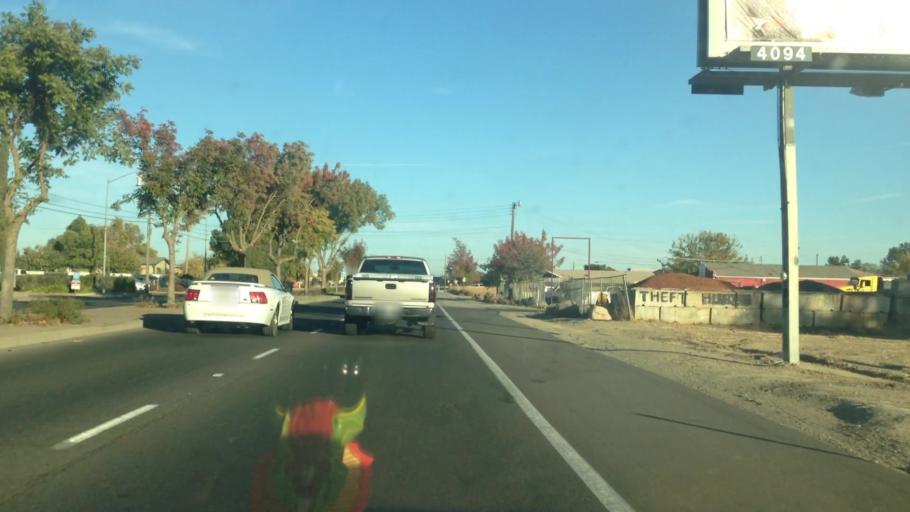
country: US
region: California
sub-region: Sacramento County
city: North Highlands
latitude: 38.6902
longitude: -121.3902
